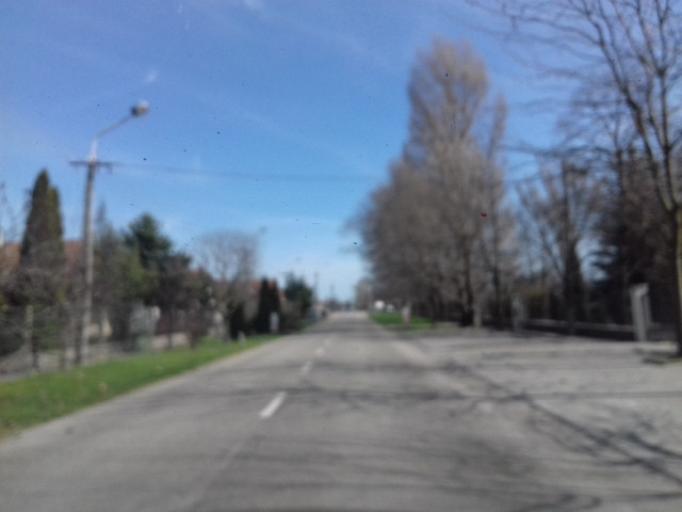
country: HU
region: Bacs-Kiskun
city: Kecskemet
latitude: 46.8949
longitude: 19.7278
